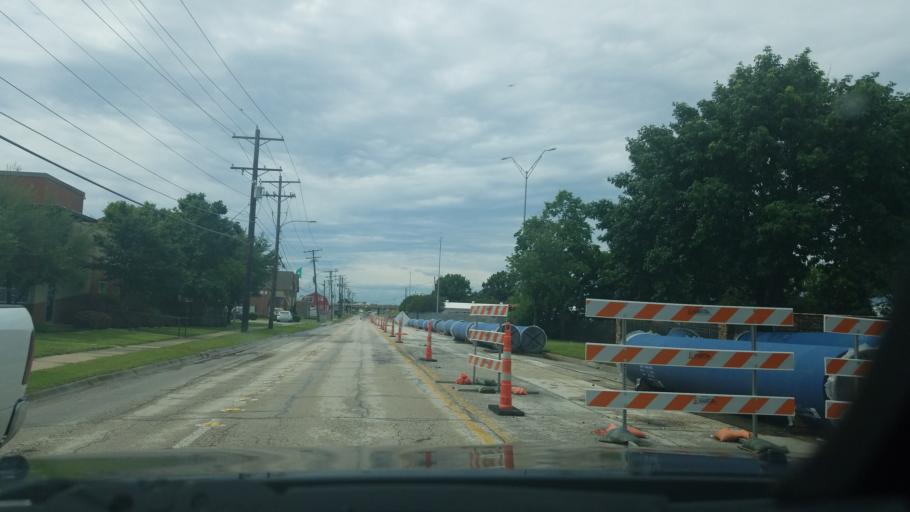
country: US
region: Texas
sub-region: Denton County
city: Denton
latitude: 33.2128
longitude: -97.1614
